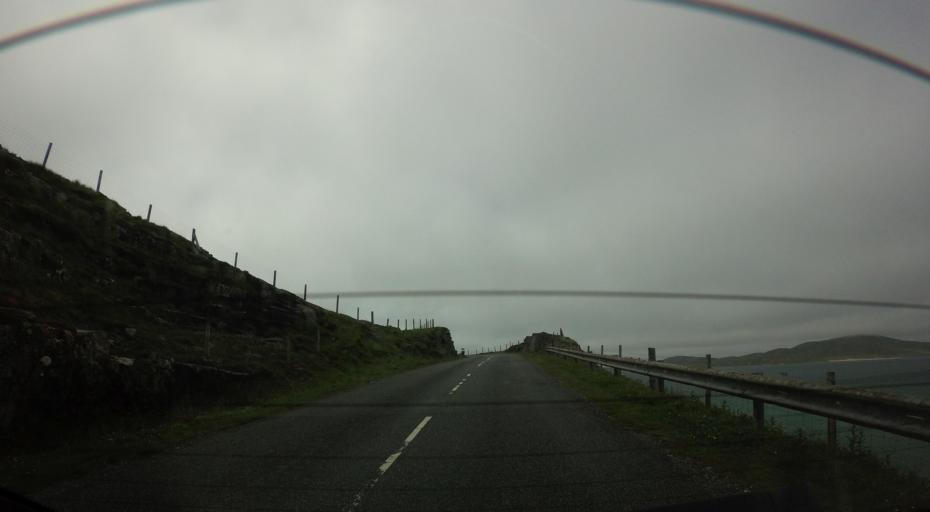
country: GB
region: Scotland
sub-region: Eilean Siar
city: Harris
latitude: 57.8673
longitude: -6.9634
